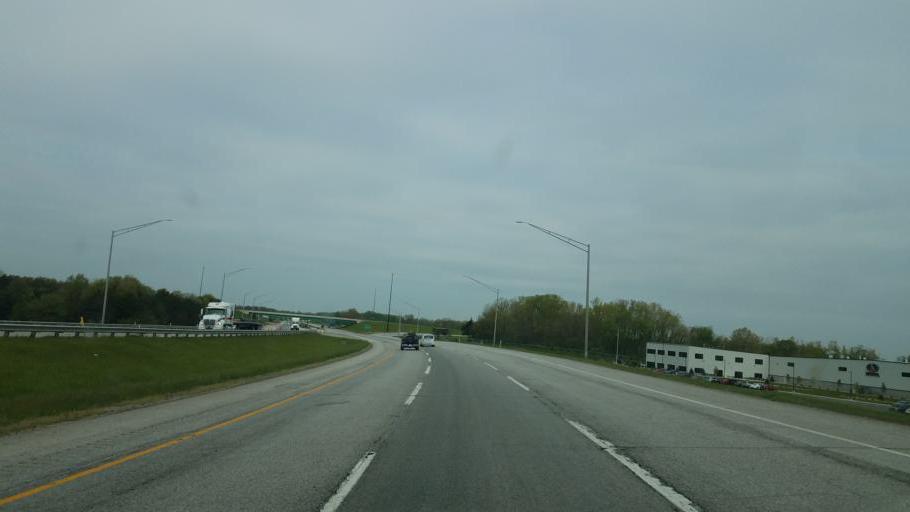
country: US
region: Indiana
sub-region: Elkhart County
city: Bristol
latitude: 41.7353
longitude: -85.7844
